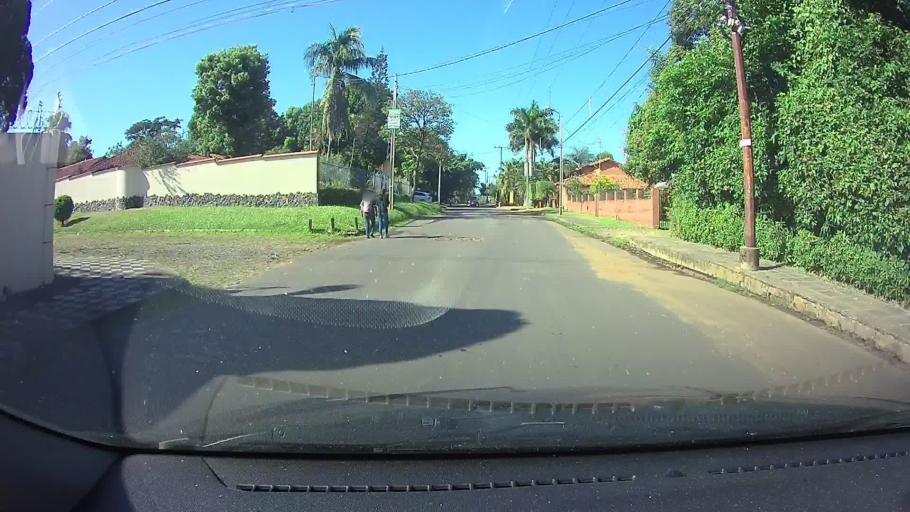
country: PY
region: Central
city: Fernando de la Mora
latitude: -25.2648
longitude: -57.5139
